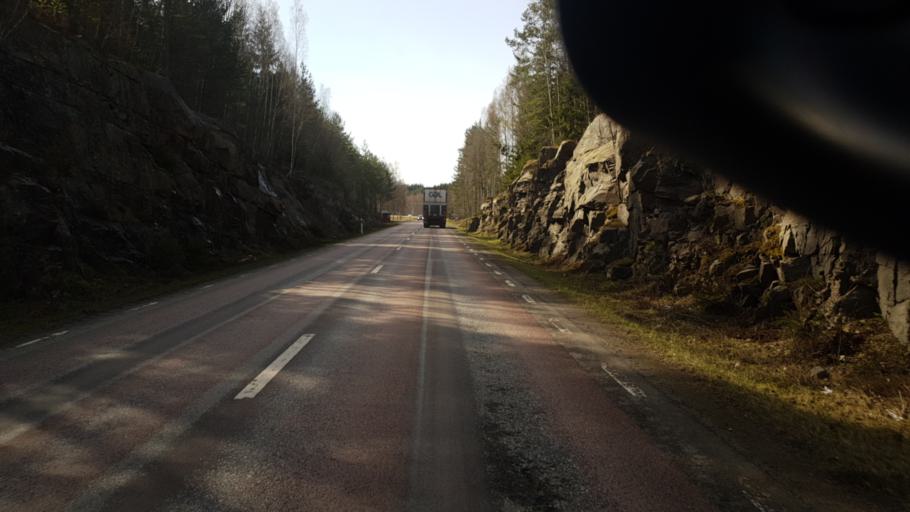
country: SE
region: Vaermland
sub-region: Arvika Kommun
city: Arvika
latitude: 59.5601
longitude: 12.7235
